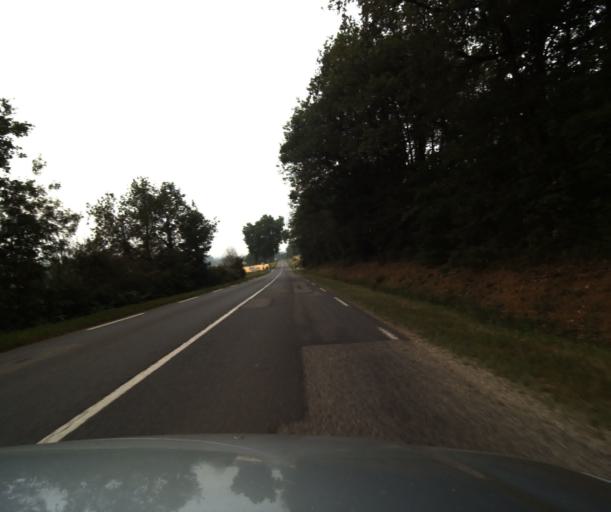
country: FR
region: Midi-Pyrenees
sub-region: Departement du Tarn-et-Garonne
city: Beaumont-de-Lomagne
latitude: 43.8177
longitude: 0.9079
